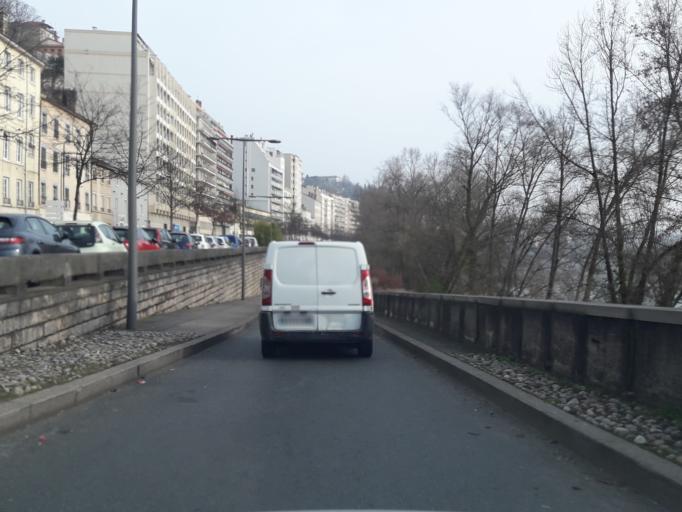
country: FR
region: Rhone-Alpes
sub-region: Departement du Rhone
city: Caluire-et-Cuire
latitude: 45.7794
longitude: 4.8415
